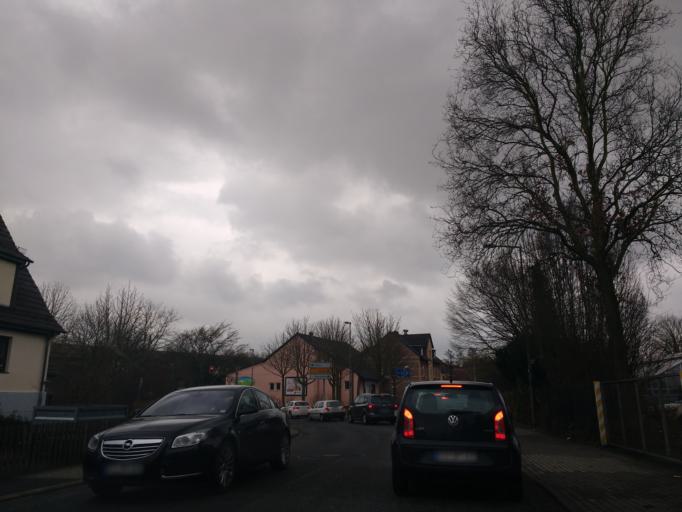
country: DE
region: Hesse
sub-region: Regierungsbezirk Kassel
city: Fuldabruck
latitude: 51.2804
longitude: 9.4534
